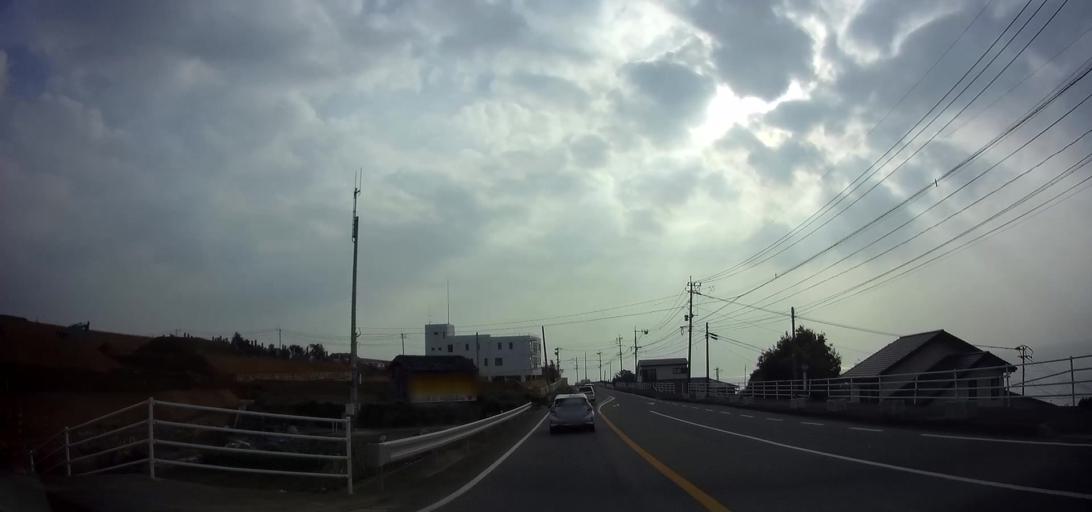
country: JP
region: Nagasaki
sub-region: Isahaya-shi
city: Isahaya
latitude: 32.7912
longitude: 130.0647
